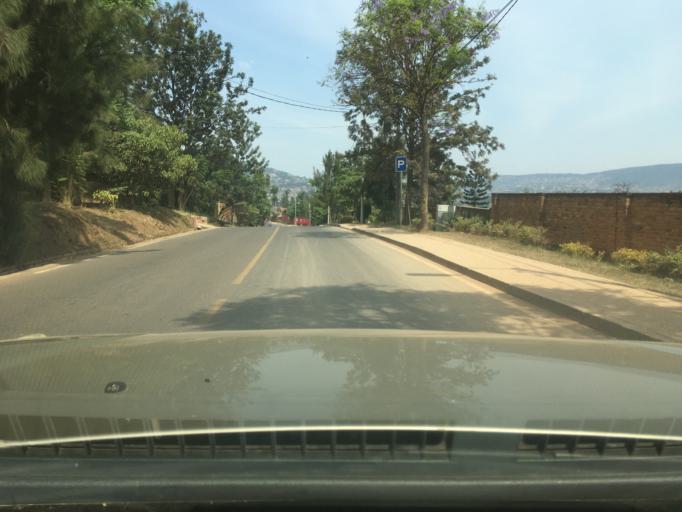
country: RW
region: Kigali
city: Kigali
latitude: -1.9623
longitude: 30.1029
